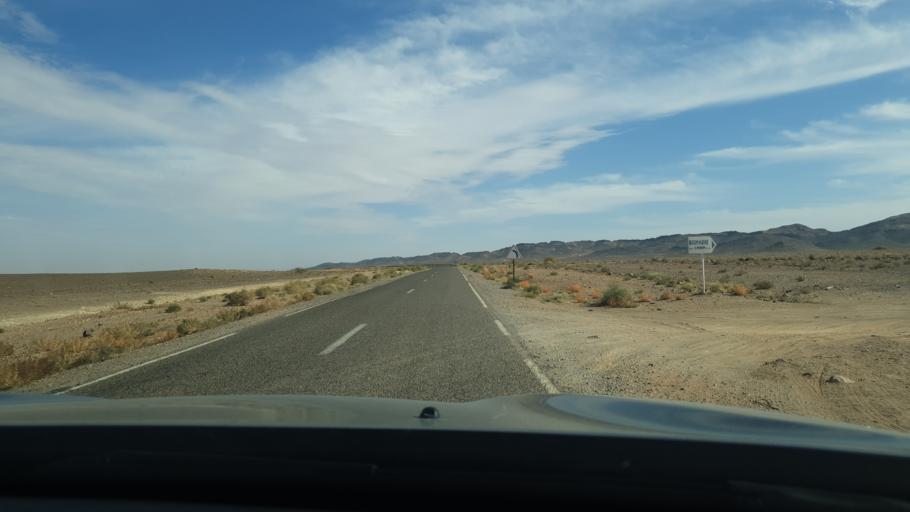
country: MA
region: Meknes-Tafilalet
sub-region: Errachidia
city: Goulmima
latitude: 31.5101
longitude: -4.9910
